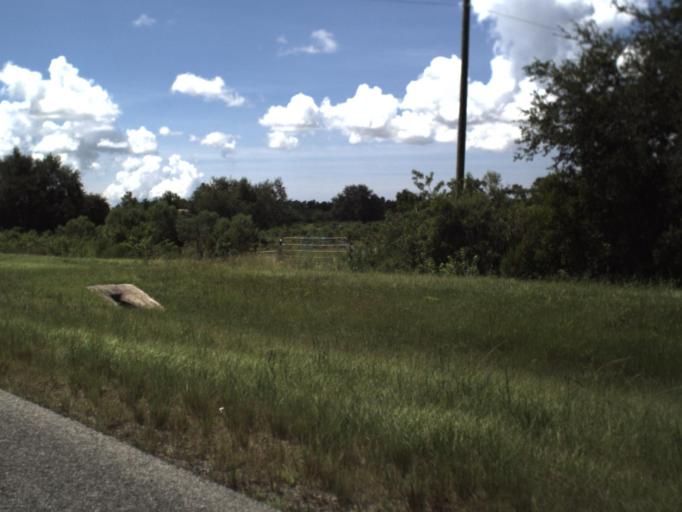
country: US
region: Florida
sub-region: Charlotte County
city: Harbour Heights
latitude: 27.0098
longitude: -81.9588
